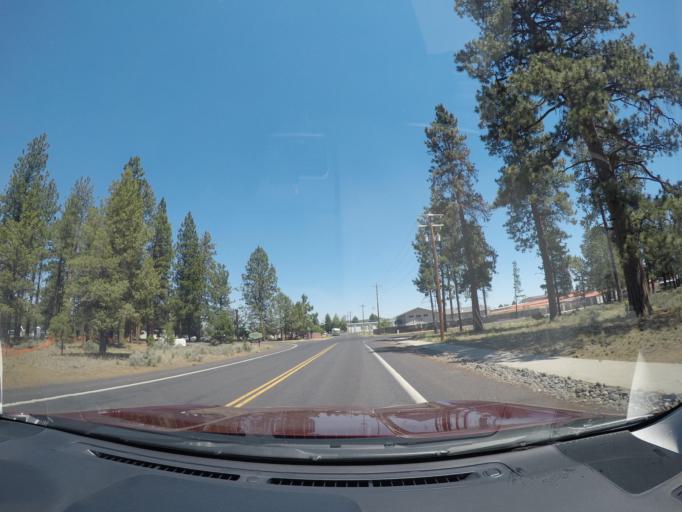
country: US
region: Oregon
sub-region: Deschutes County
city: Sisters
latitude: 44.2970
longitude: -121.5547
